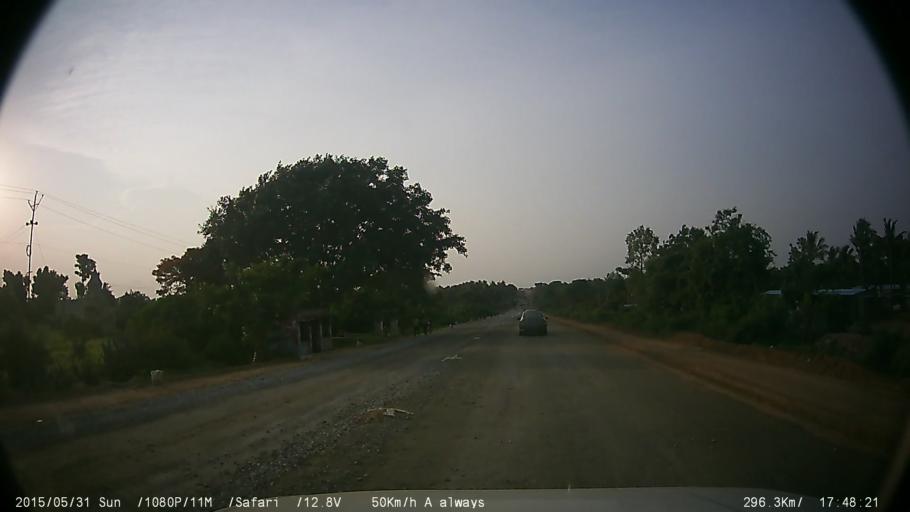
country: IN
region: Karnataka
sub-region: Mysore
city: Nanjangud
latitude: 11.9655
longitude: 76.6703
